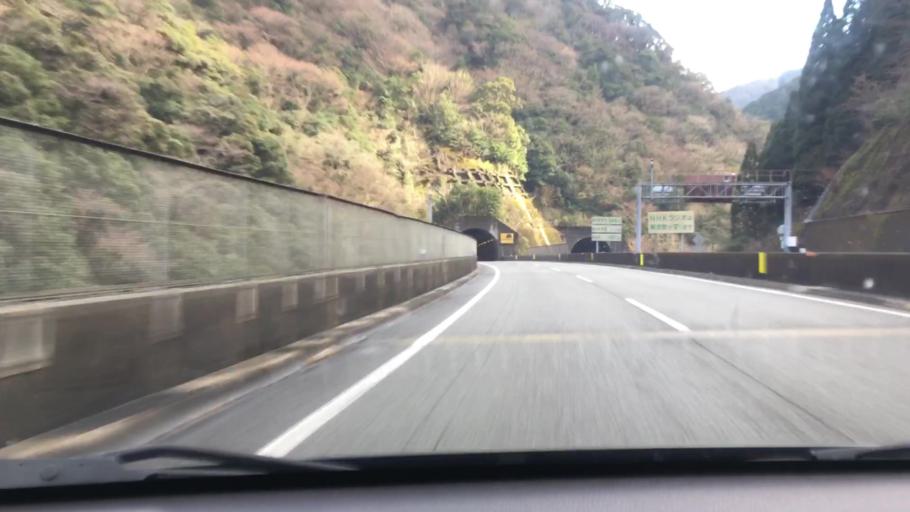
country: JP
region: Kumamoto
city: Hitoyoshi
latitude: 32.3381
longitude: 130.7325
